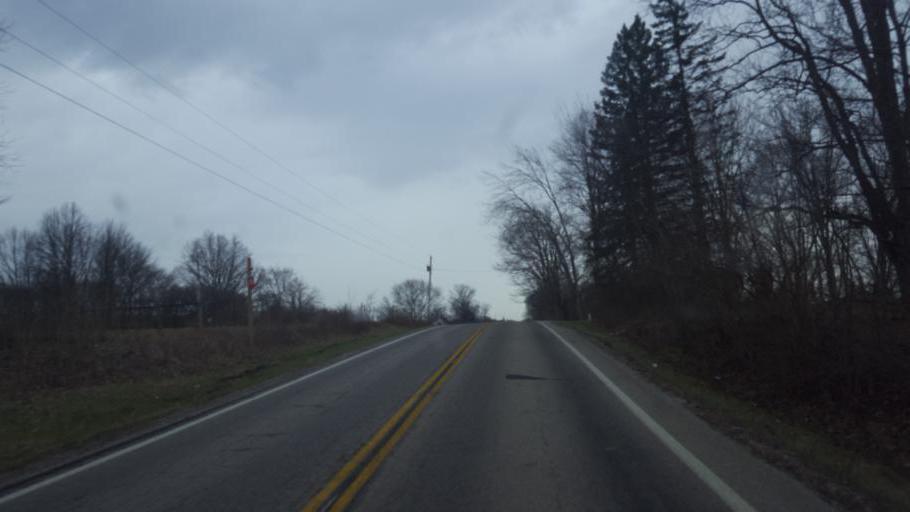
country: US
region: Ohio
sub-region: Morrow County
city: Mount Gilead
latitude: 40.4907
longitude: -82.8202
